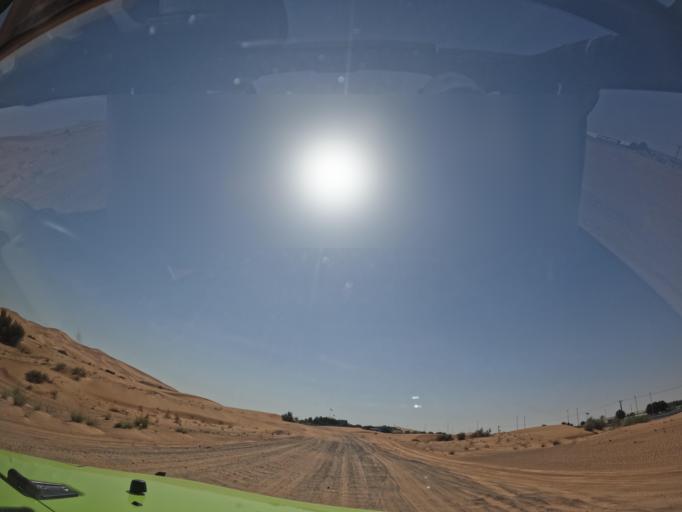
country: AE
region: Ash Shariqah
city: Adh Dhayd
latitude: 24.9609
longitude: 55.7098
